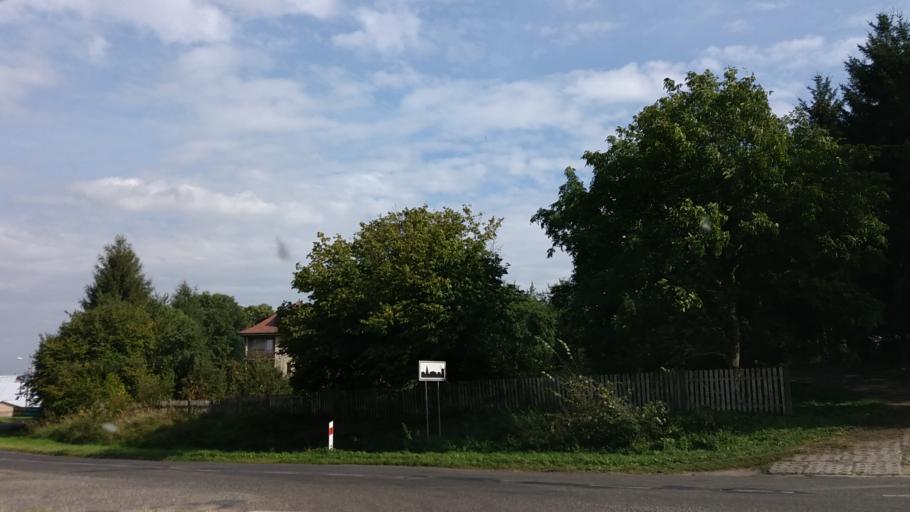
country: PL
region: West Pomeranian Voivodeship
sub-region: Powiat stargardzki
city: Suchan
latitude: 53.2237
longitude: 15.2978
